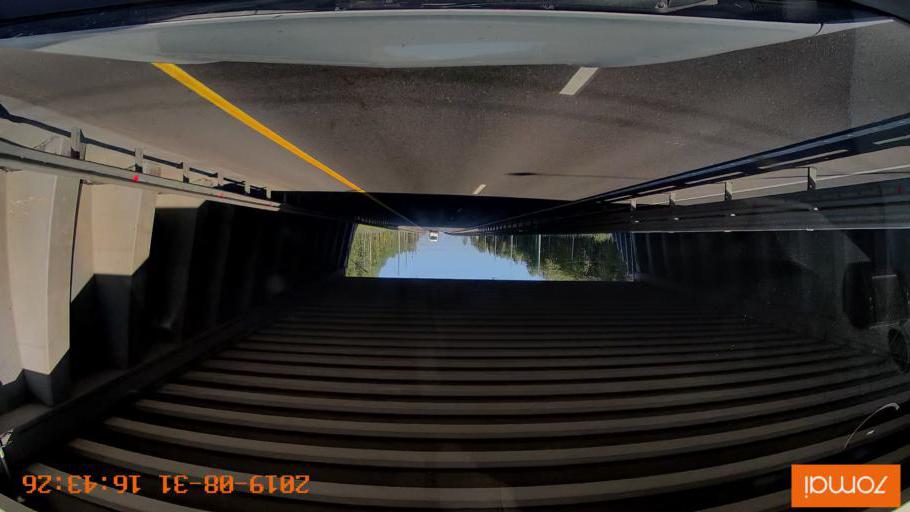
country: RU
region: Kaluga
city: Mstikhino
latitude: 54.6092
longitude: 36.1043
